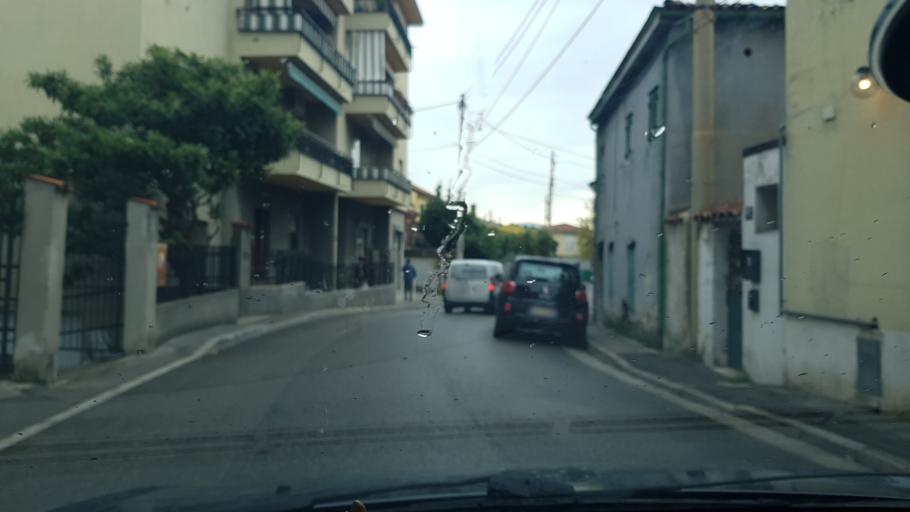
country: IT
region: Friuli Venezia Giulia
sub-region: Provincia di Trieste
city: Trieste
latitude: 45.6248
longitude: 13.7843
